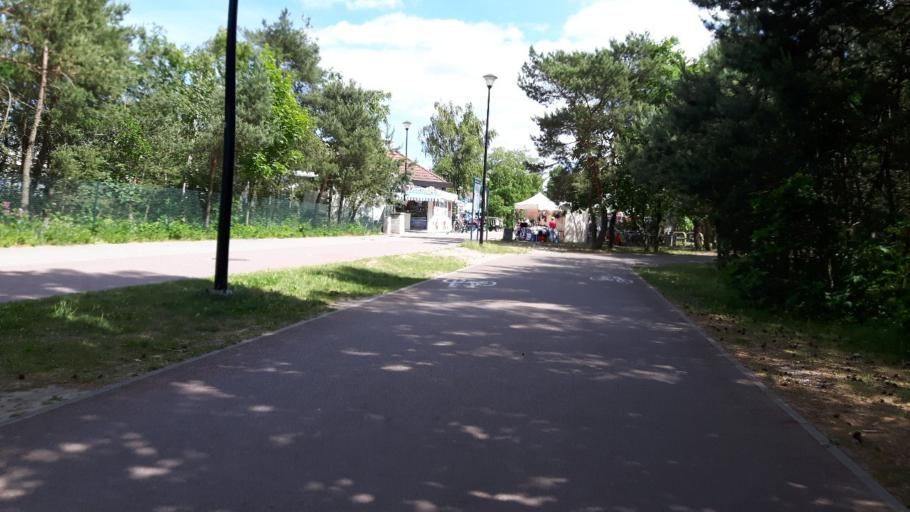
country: PL
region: Pomeranian Voivodeship
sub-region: Gdansk
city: Gdansk
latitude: 54.4136
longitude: 18.6232
